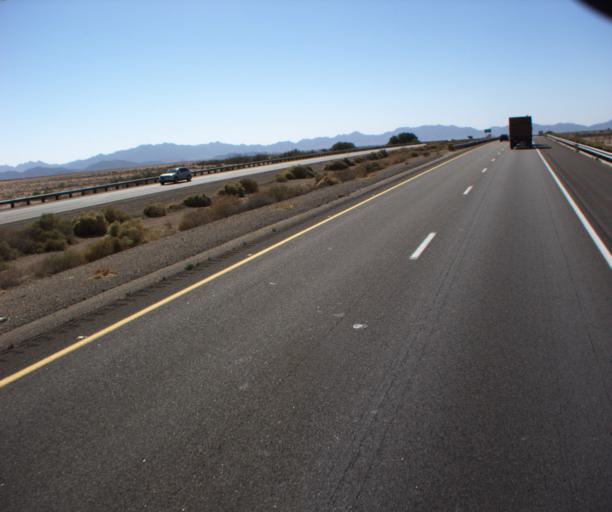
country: US
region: Arizona
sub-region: Yuma County
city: Wellton
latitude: 32.6770
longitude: -114.0453
